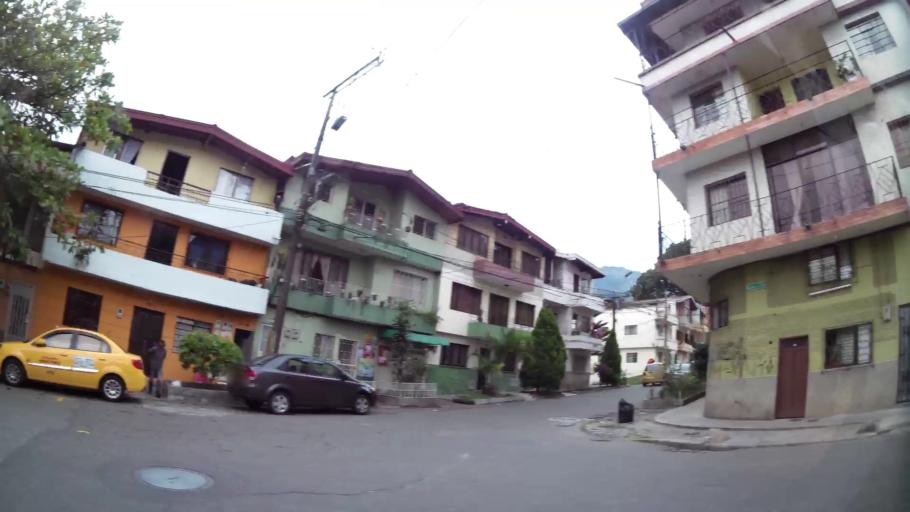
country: CO
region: Antioquia
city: Medellin
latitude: 6.2413
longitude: -75.5505
